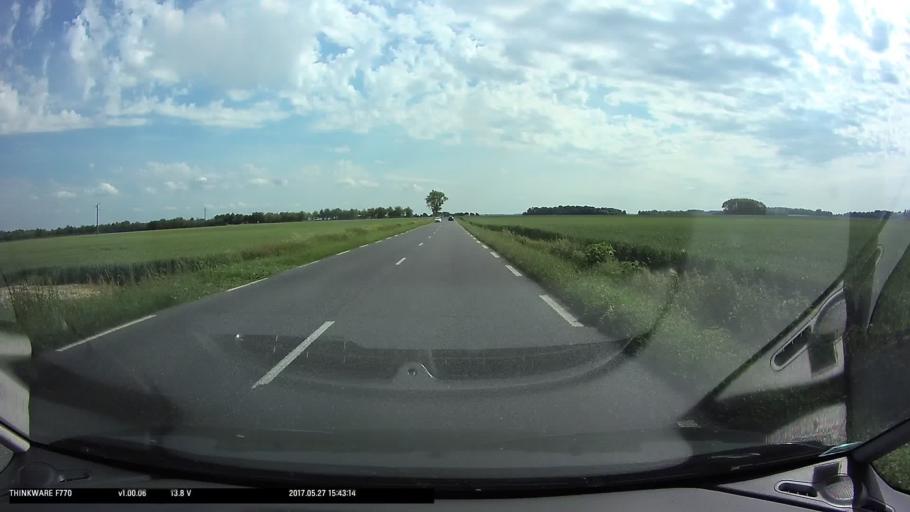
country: FR
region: Picardie
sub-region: Departement de l'Oise
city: Chaumont-en-Vexin
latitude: 49.2070
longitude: 1.8809
